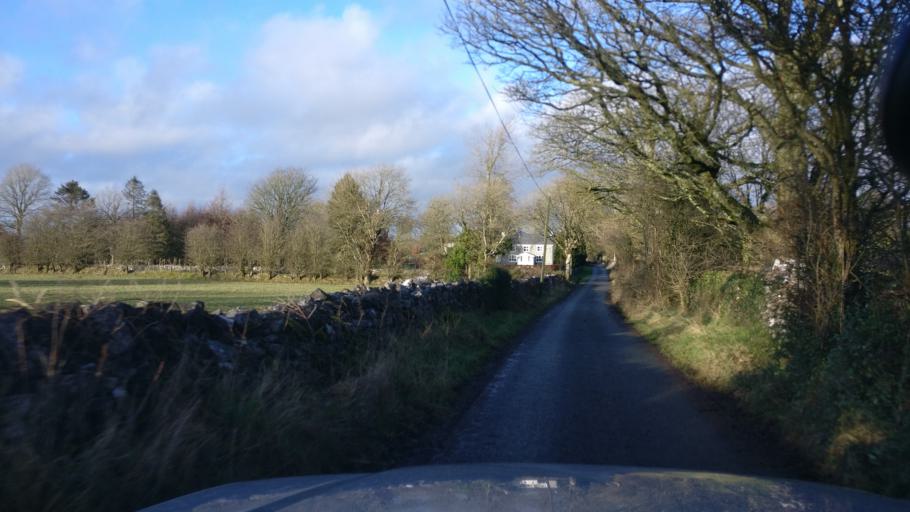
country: IE
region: Connaught
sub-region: County Galway
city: Loughrea
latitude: 53.2375
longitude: -8.5768
